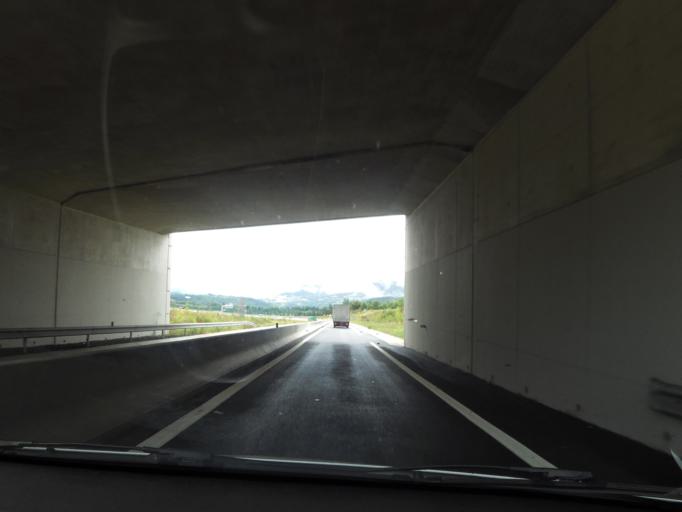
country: FR
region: Languedoc-Roussillon
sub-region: Departement de la Lozere
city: Chirac
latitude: 44.4987
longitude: 3.2385
